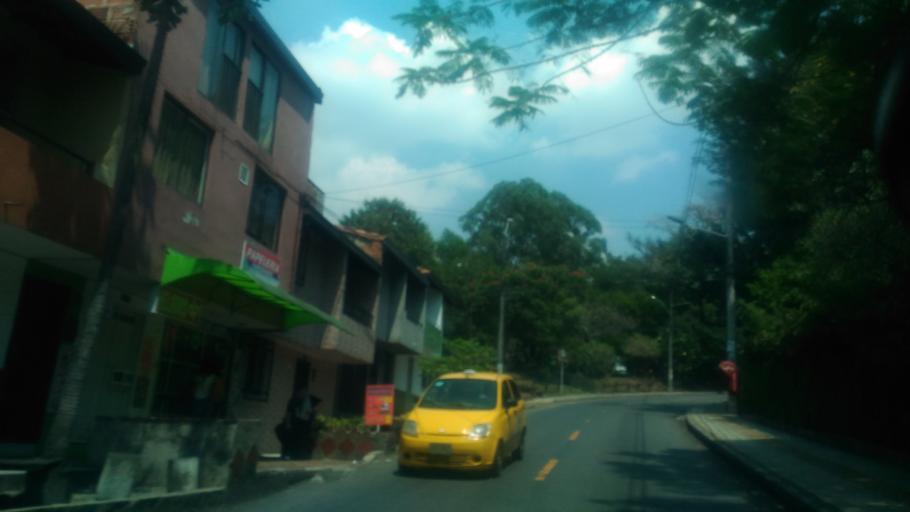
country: CO
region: Antioquia
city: Medellin
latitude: 6.2779
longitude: -75.5912
